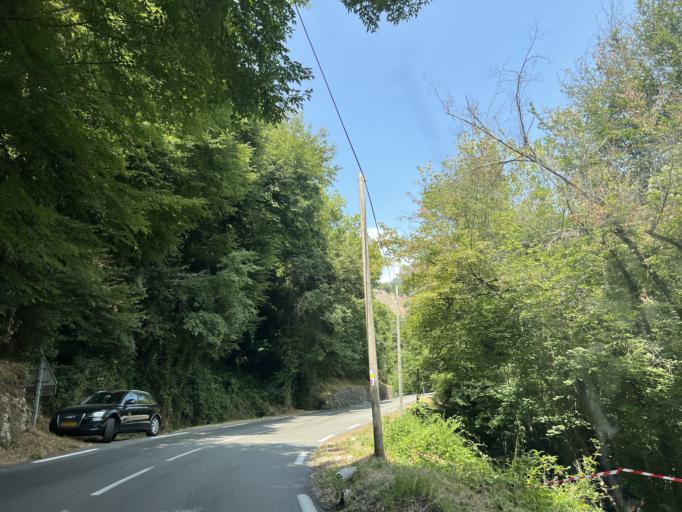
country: FR
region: Provence-Alpes-Cote d'Azur
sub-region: Departement des Alpes-Maritimes
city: Tourrettes-sur-Loup
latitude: 43.7483
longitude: 6.9965
